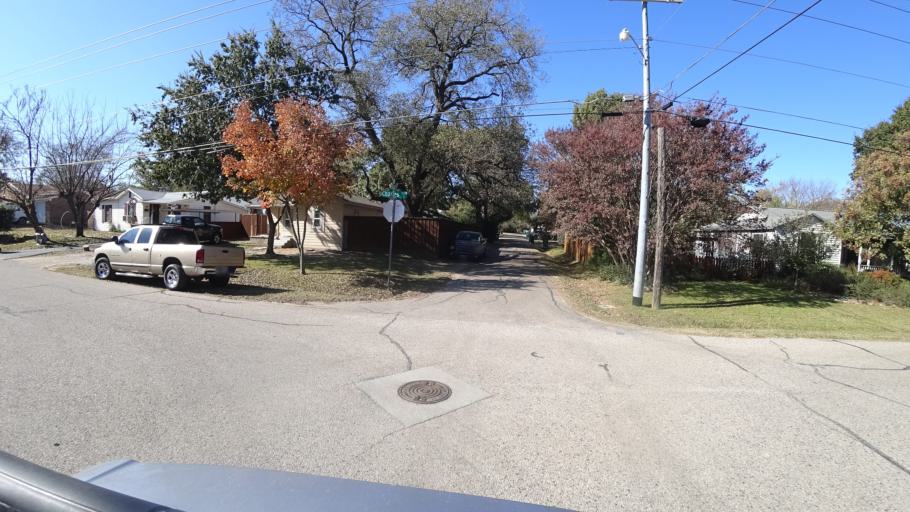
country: US
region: Texas
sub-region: Denton County
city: Lewisville
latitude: 33.0500
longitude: -96.9964
